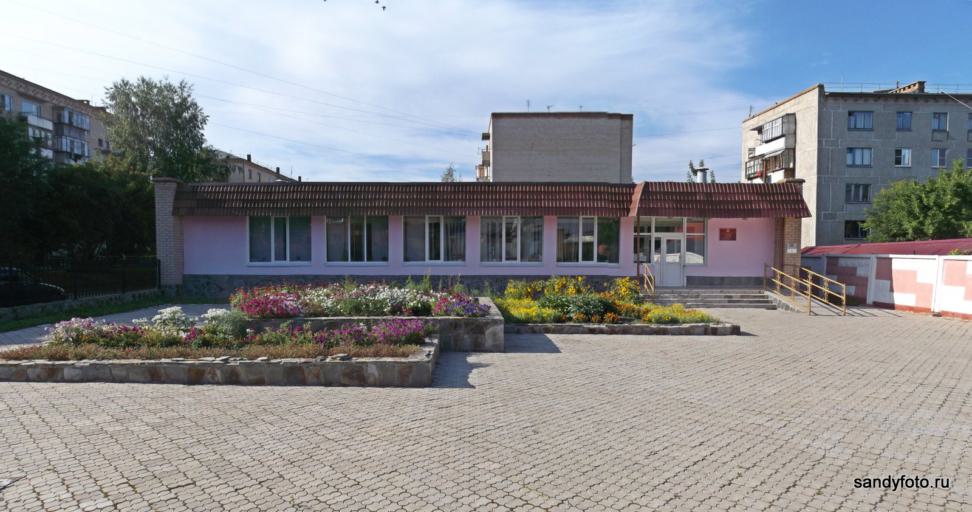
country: RU
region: Chelyabinsk
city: Troitsk
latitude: 54.0871
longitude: 61.5449
